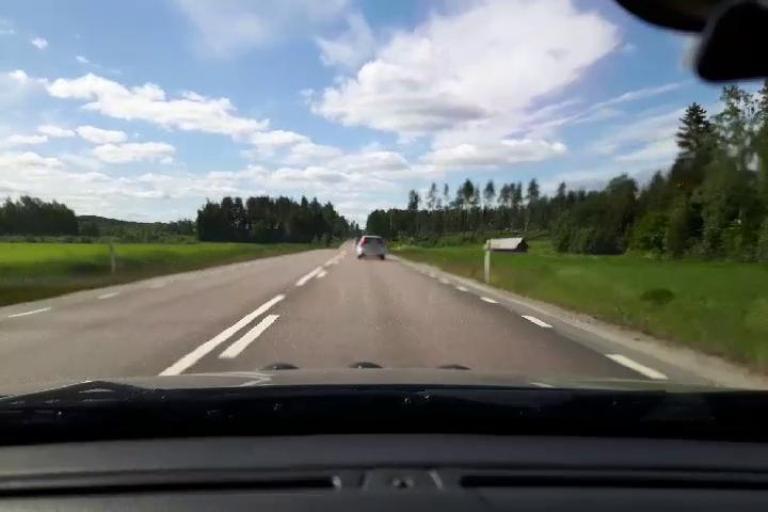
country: SE
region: Gaevleborg
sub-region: Bollnas Kommun
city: Bollnas
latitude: 61.3204
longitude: 16.4317
